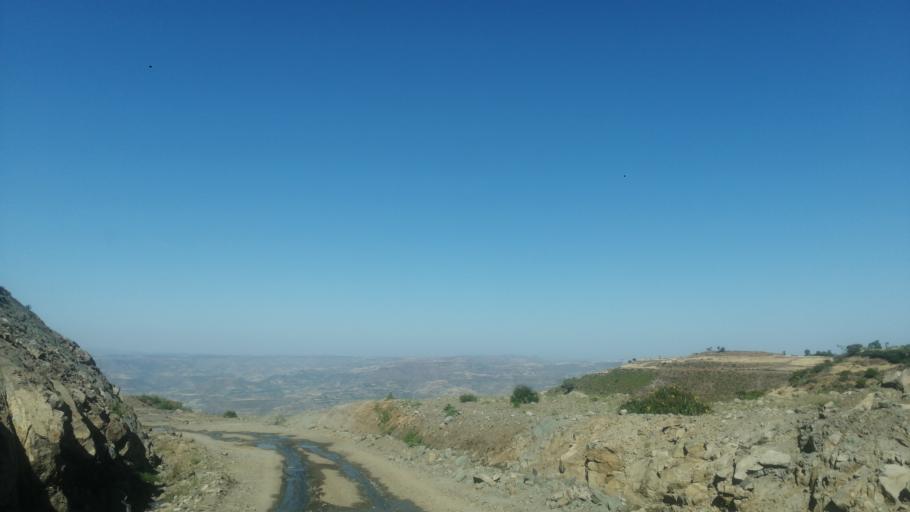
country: ET
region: Amhara
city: Addiet Canna
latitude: 11.1522
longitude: 37.8604
